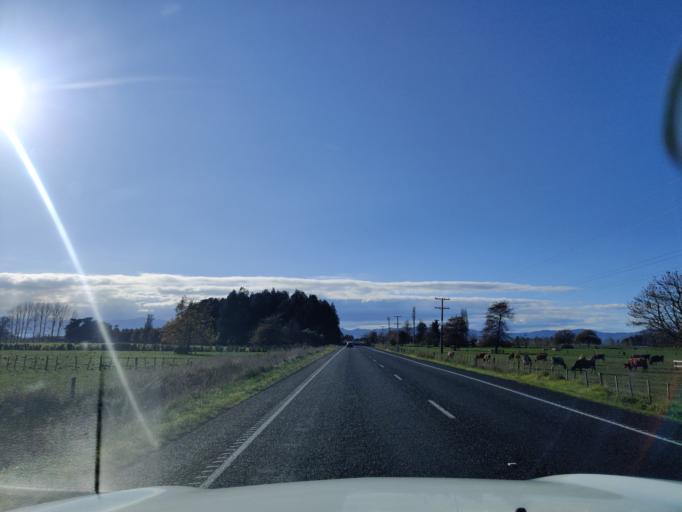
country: NZ
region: Waikato
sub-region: Hauraki District
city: Ngatea
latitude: -37.2727
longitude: 175.5187
